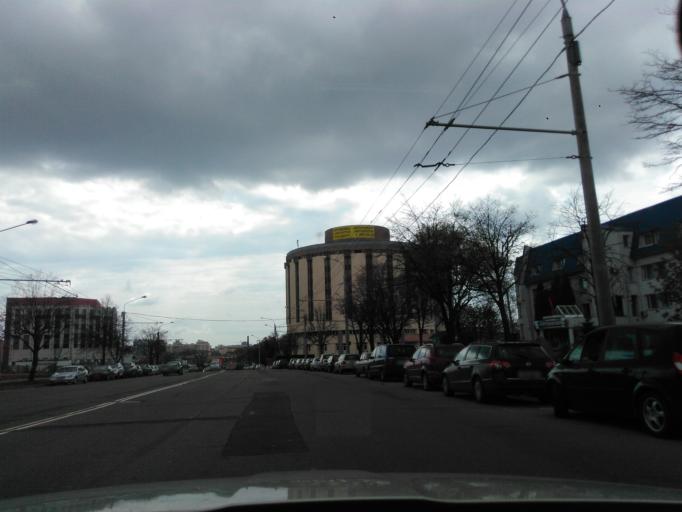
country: BY
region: Minsk
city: Minsk
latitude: 53.9018
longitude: 27.5340
